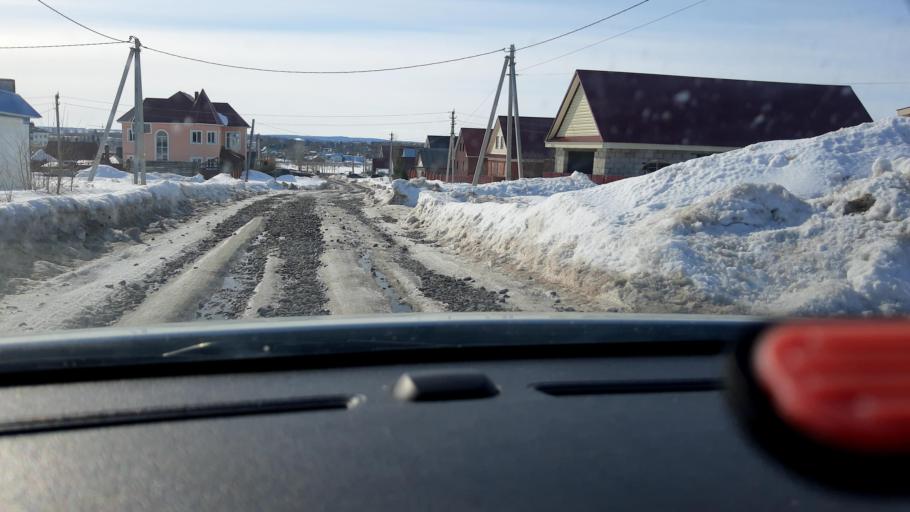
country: RU
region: Bashkortostan
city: Chishmy
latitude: 54.6063
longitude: 55.3863
